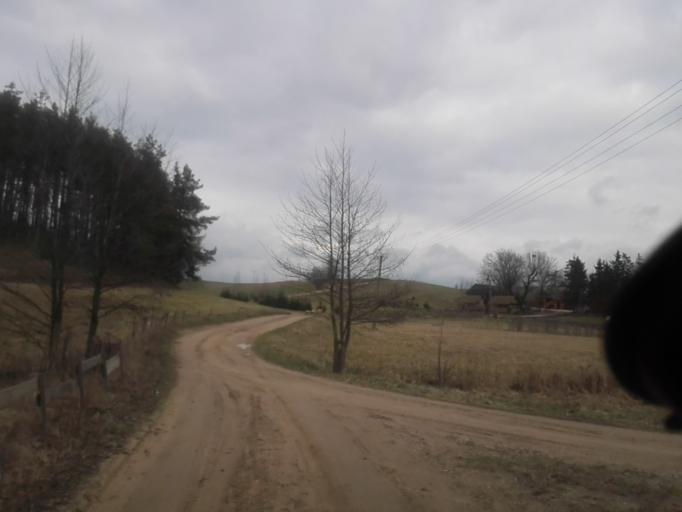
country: PL
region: Podlasie
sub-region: Suwalki
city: Suwalki
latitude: 54.2526
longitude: 22.9411
